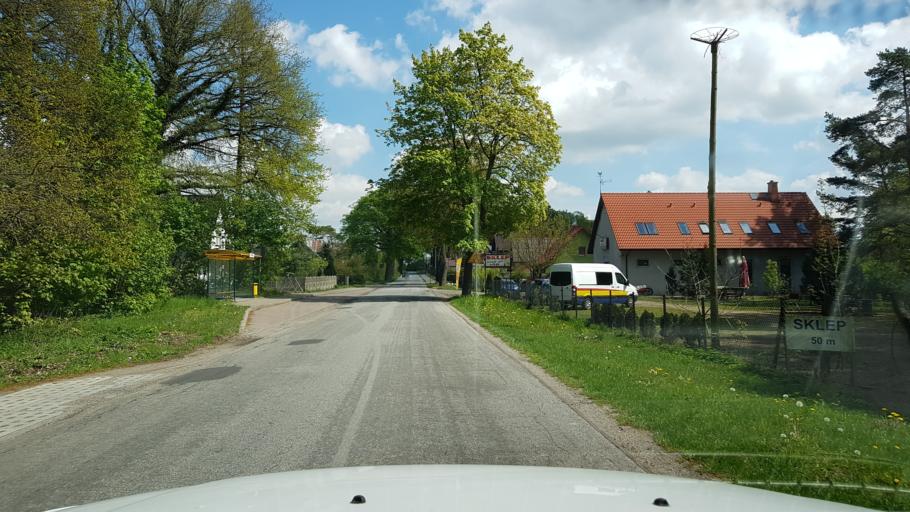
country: PL
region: West Pomeranian Voivodeship
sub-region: Powiat slawienski
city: Slawno
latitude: 54.4725
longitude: 16.6274
